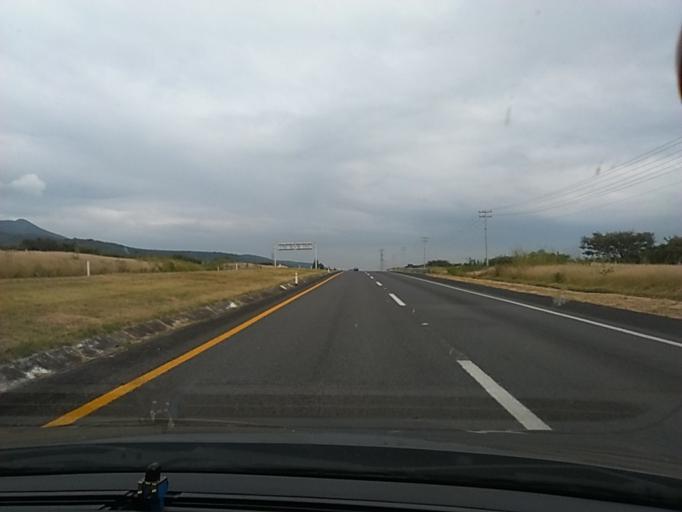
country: MX
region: Michoacan
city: Churintzio
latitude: 20.1288
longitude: -102.0648
